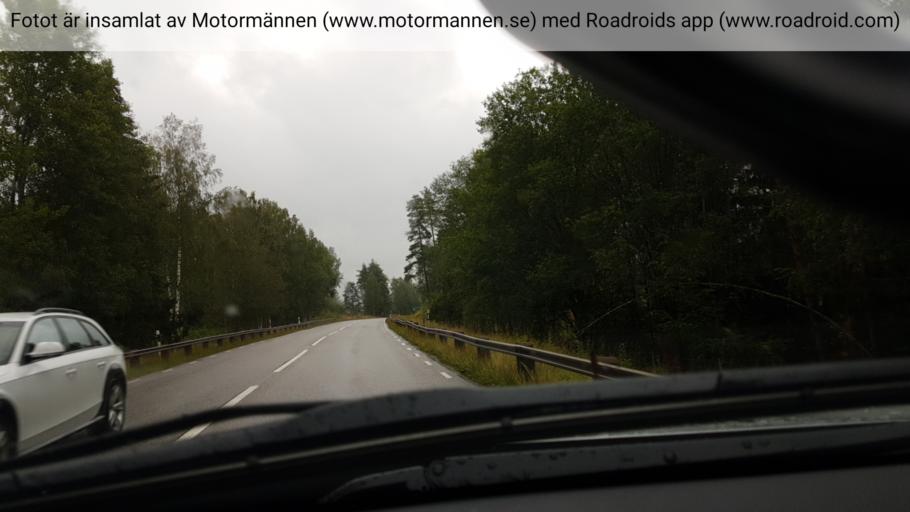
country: SE
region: Vaestra Goetaland
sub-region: Bengtsfors Kommun
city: Billingsfors
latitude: 58.9678
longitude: 12.2354
